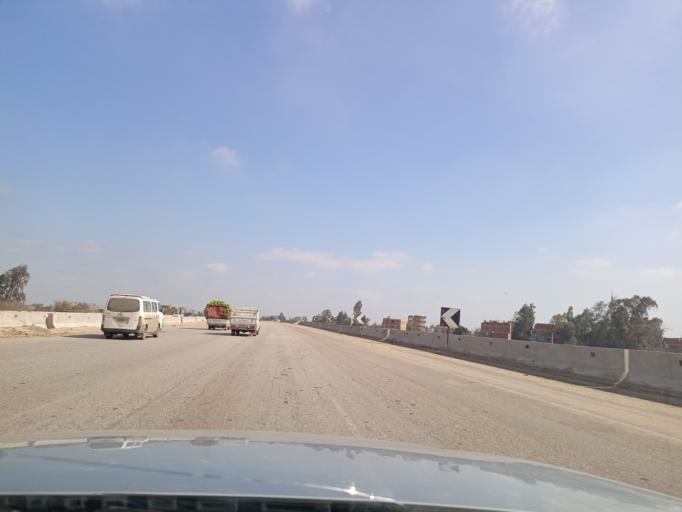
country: EG
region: Muhafazat al Minufiyah
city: Al Bajur
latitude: 30.4231
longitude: 31.0875
